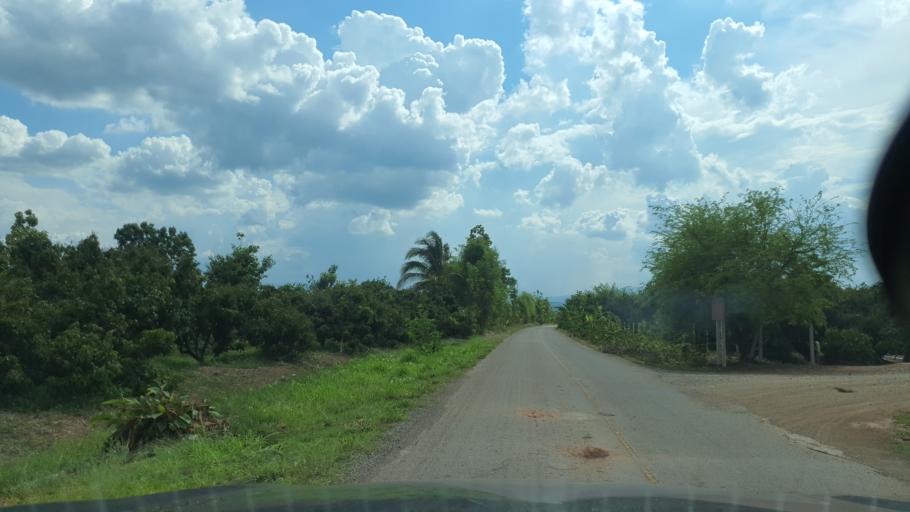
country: TH
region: Chiang Mai
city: Mae Taeng
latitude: 19.1314
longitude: 99.0419
